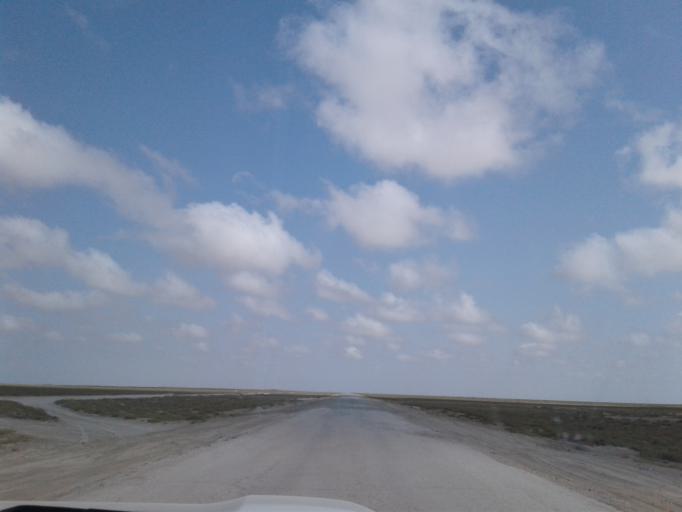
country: IR
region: Golestan
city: Gomishan
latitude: 37.6002
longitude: 53.9242
